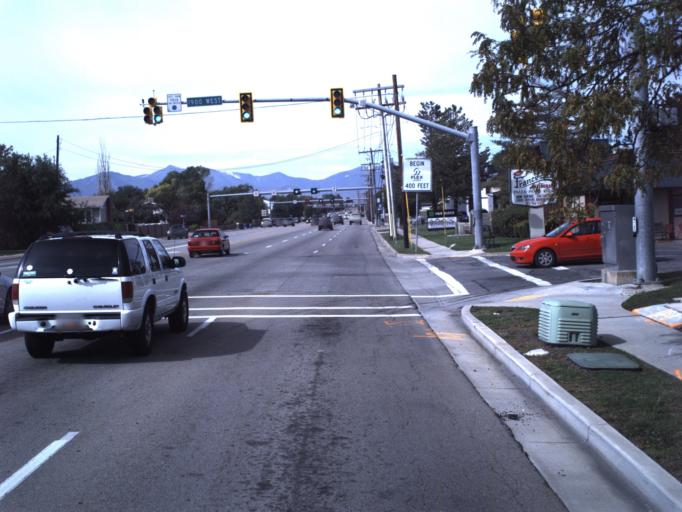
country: US
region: Utah
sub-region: Salt Lake County
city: Taylorsville
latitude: 40.6532
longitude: -111.9426
